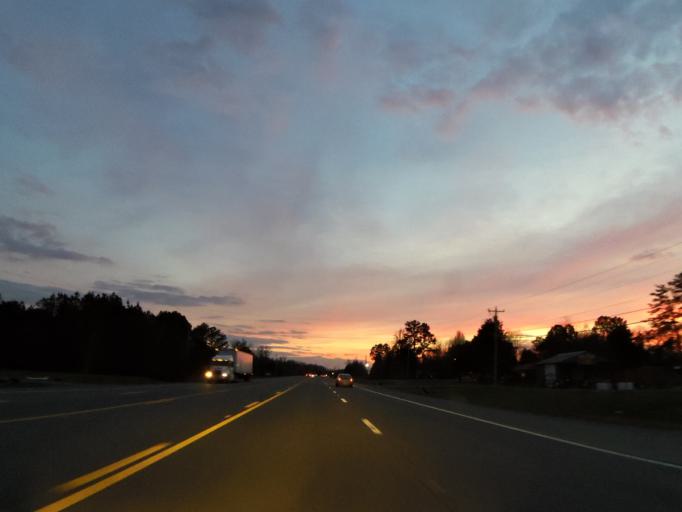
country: US
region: Tennessee
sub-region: Polk County
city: Benton
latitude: 35.1528
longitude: -84.7045
